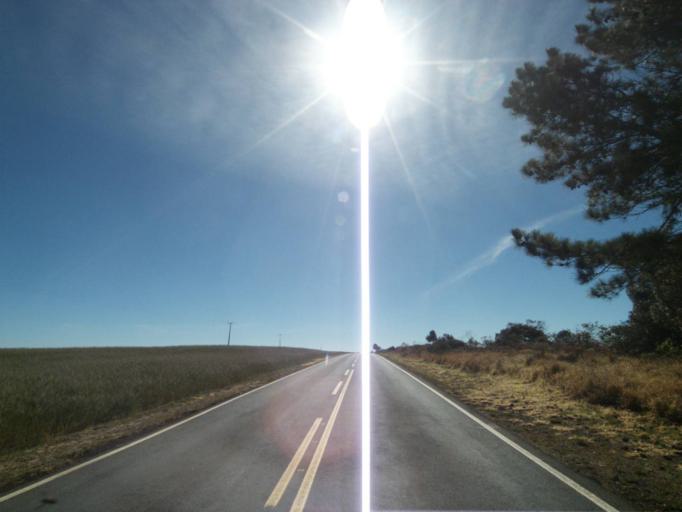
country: BR
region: Parana
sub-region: Castro
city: Castro
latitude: -24.7058
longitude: -50.1938
